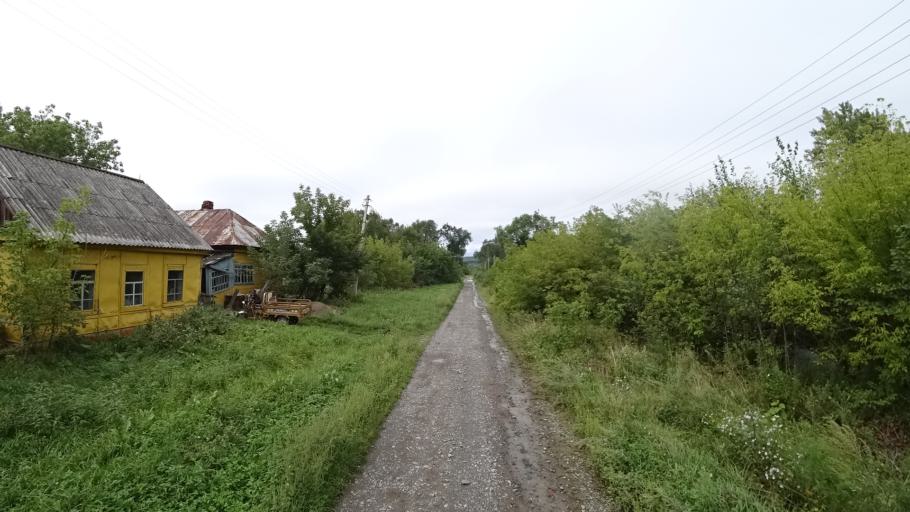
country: RU
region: Primorskiy
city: Lyalichi
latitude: 44.0786
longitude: 132.4819
